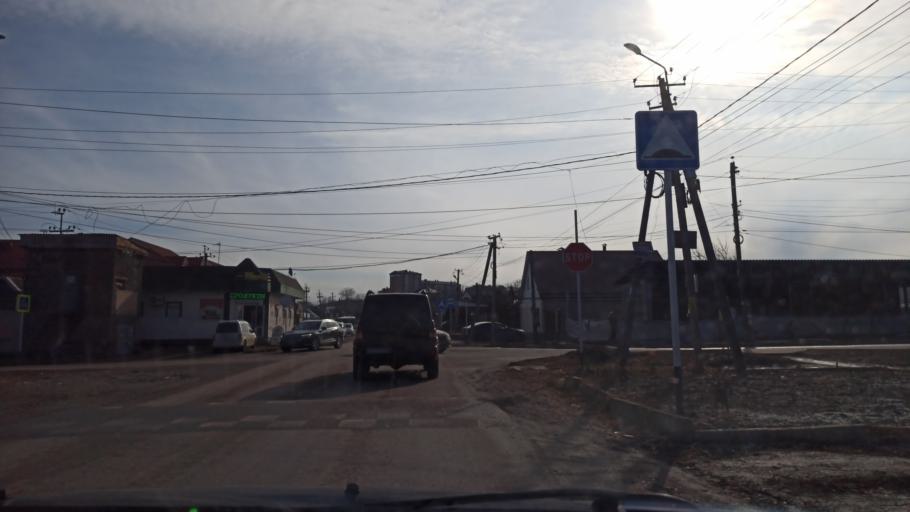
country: RU
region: Stavropol'skiy
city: Yessentukskaya
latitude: 44.0262
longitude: 42.8653
